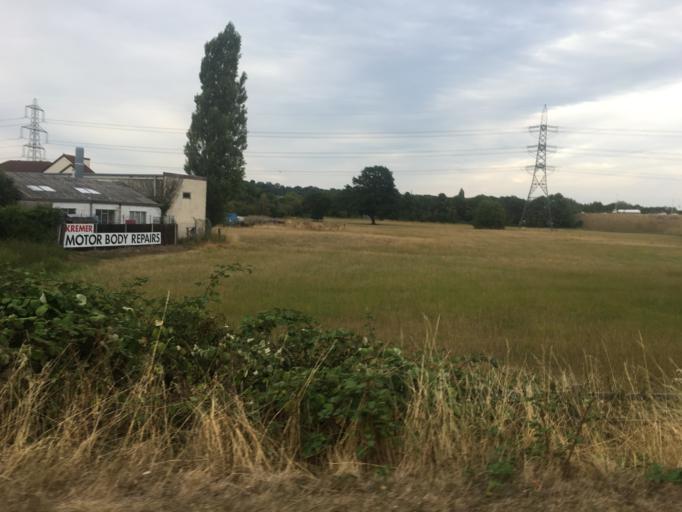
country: GB
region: England
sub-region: West Berkshire
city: Theale
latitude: 51.4376
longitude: -1.0721
